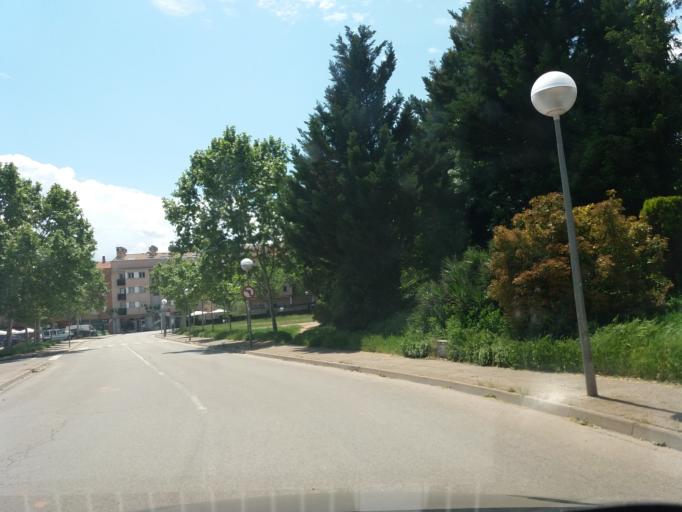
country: ES
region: Catalonia
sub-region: Provincia de Barcelona
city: Sant Joan de Vilatorrada
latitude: 41.7415
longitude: 1.8009
